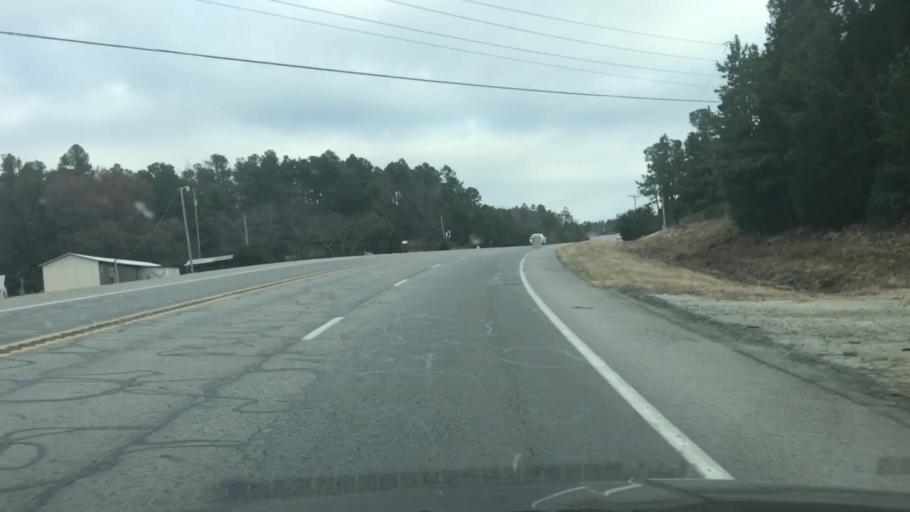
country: US
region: Arkansas
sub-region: Scott County
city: Waldron
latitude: 34.8131
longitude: -94.0402
